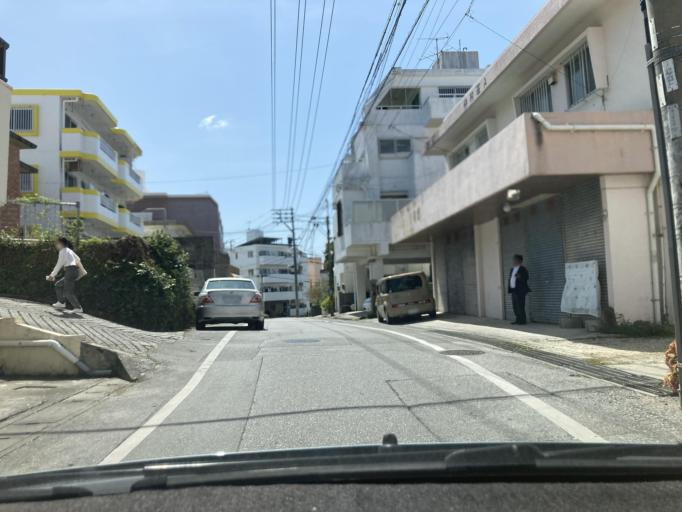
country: JP
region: Okinawa
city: Naha-shi
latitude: 26.2017
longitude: 127.6885
